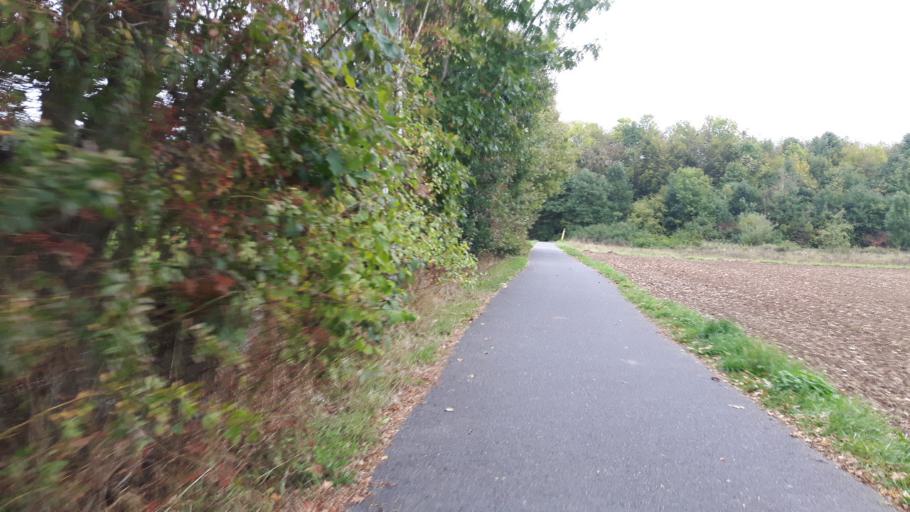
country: DE
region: North Rhine-Westphalia
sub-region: Regierungsbezirk Koln
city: Hennef
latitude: 50.7750
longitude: 7.2977
